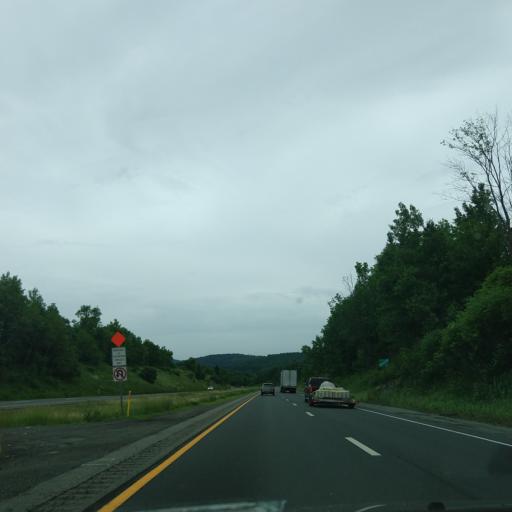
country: US
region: Pennsylvania
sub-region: Lackawanna County
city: Dalton
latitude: 41.6674
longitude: -75.6780
